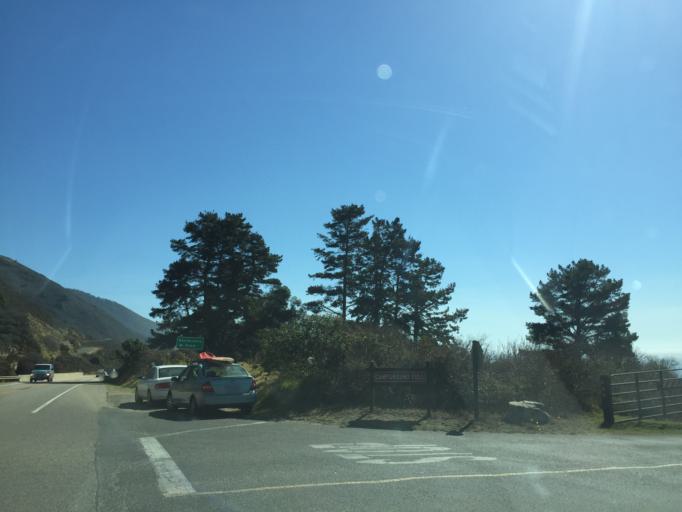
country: US
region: California
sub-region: Monterey County
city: Greenfield
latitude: 35.9901
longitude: -121.4950
